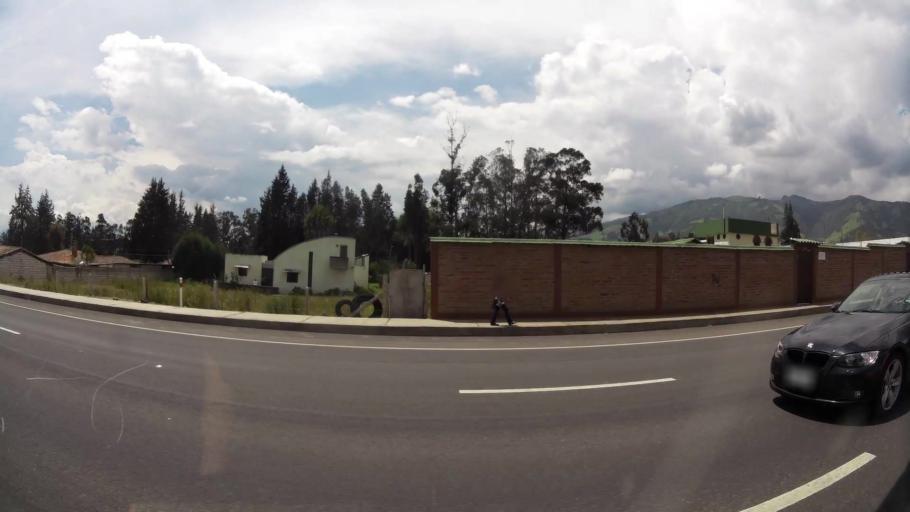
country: EC
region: Pichincha
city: Sangolqui
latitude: -0.2001
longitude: -78.3365
